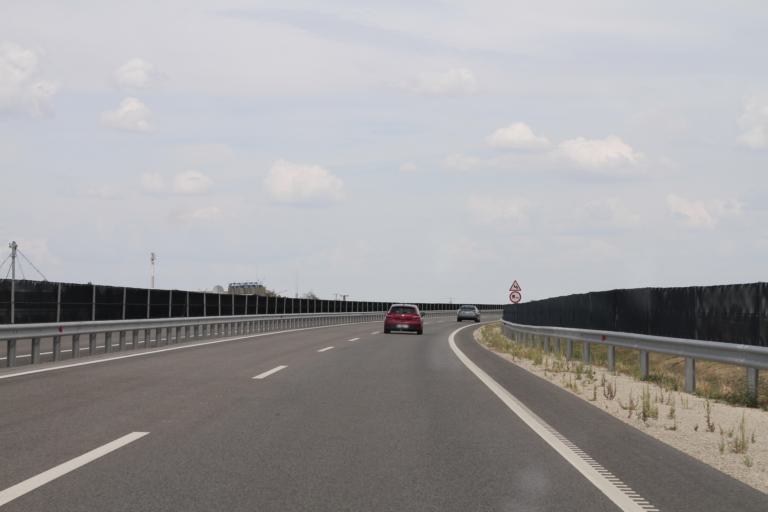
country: HU
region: Bacs-Kiskun
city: Tiszakecske
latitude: 46.8737
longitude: 20.1088
